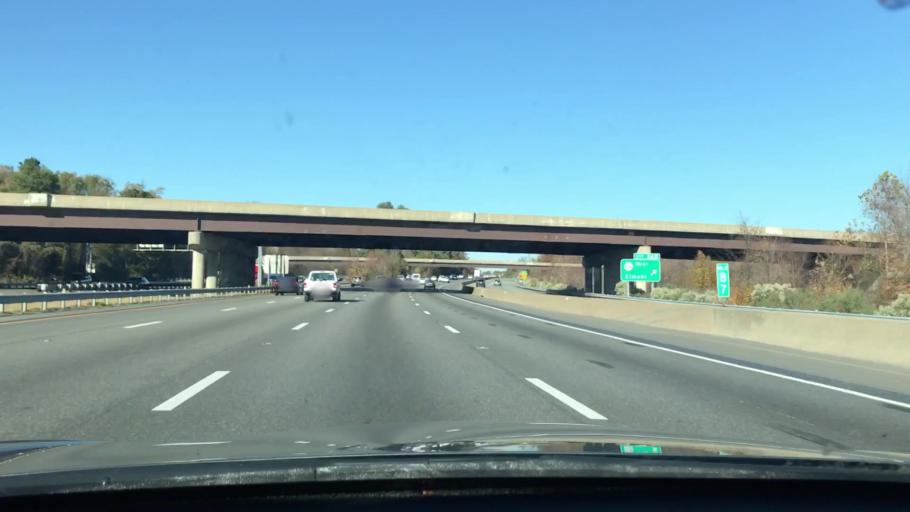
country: US
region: Virginia
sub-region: Henrico County
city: Glen Allen
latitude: 37.6872
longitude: -77.4537
